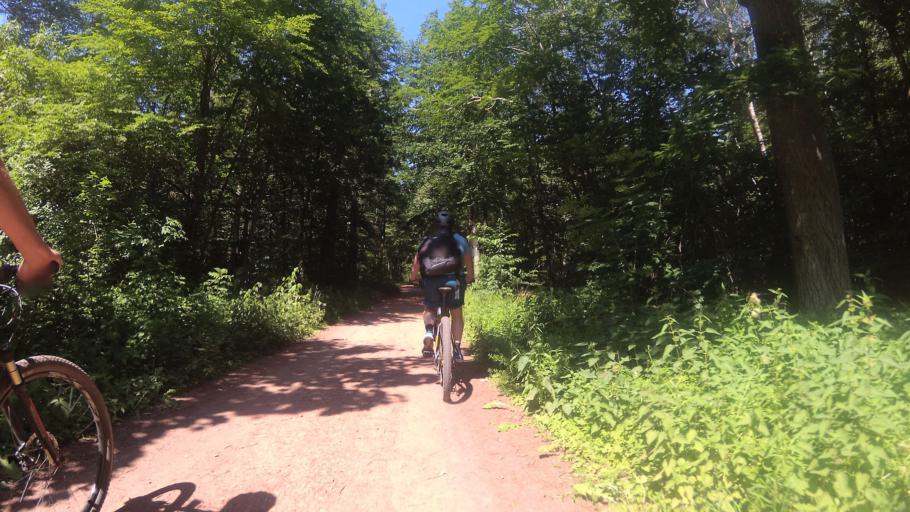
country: DE
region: Saarland
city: Beckingen
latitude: 49.3964
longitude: 6.7253
